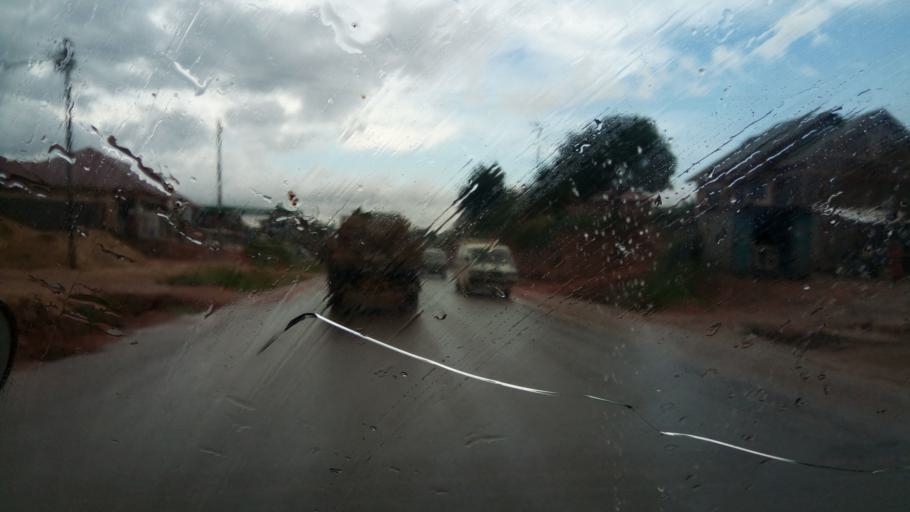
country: UG
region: Central Region
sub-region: Wakiso District
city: Wakiso
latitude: 0.3973
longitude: 32.4863
